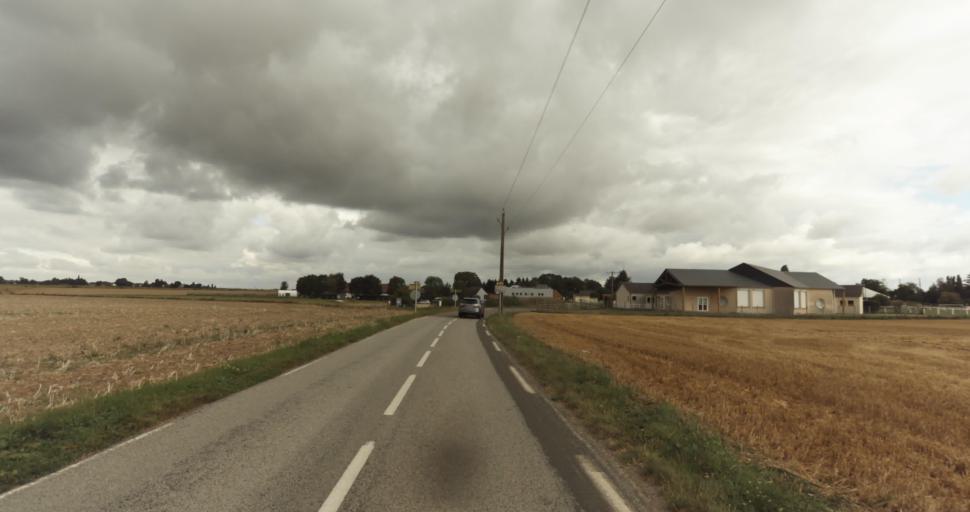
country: FR
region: Haute-Normandie
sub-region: Departement de l'Eure
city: Gravigny
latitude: 49.0014
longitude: 1.2355
